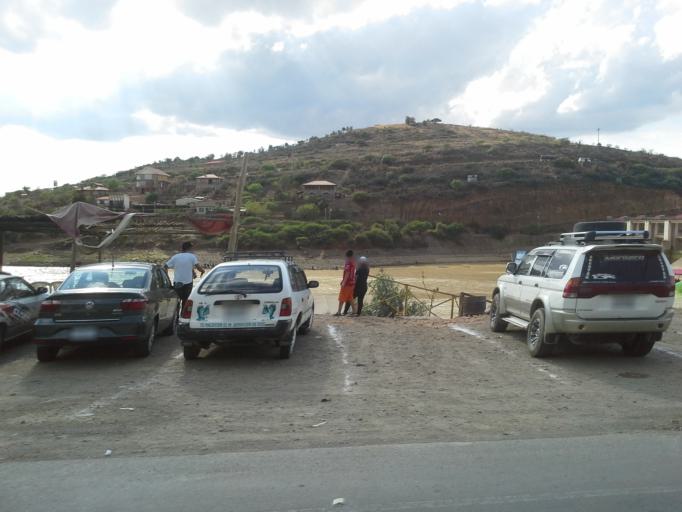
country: BO
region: Cochabamba
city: Tarata
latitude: -17.5293
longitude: -66.0848
